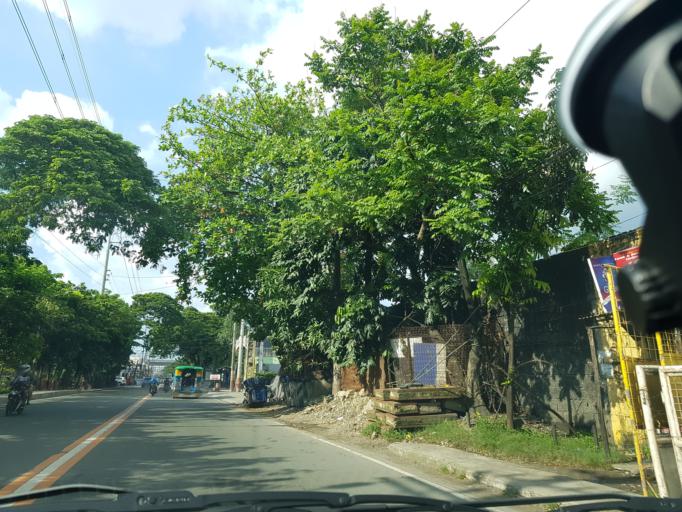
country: PH
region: Metro Manila
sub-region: Marikina
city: Calumpang
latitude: 14.6160
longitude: 121.0924
